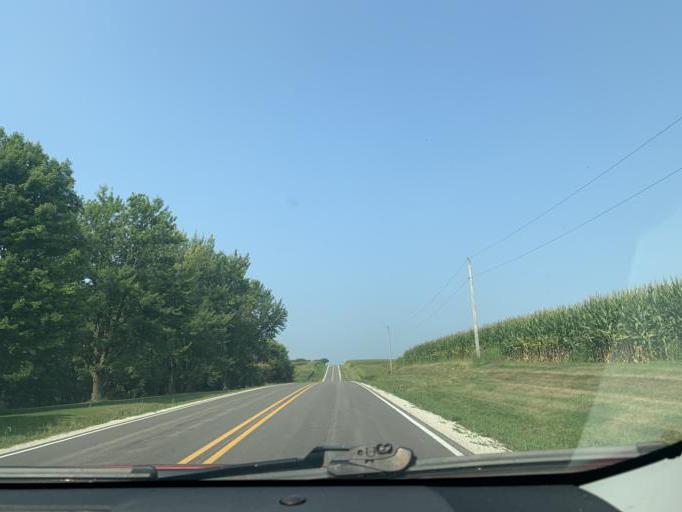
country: US
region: Illinois
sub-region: Whiteside County
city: Sterling
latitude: 41.8441
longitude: -89.7664
